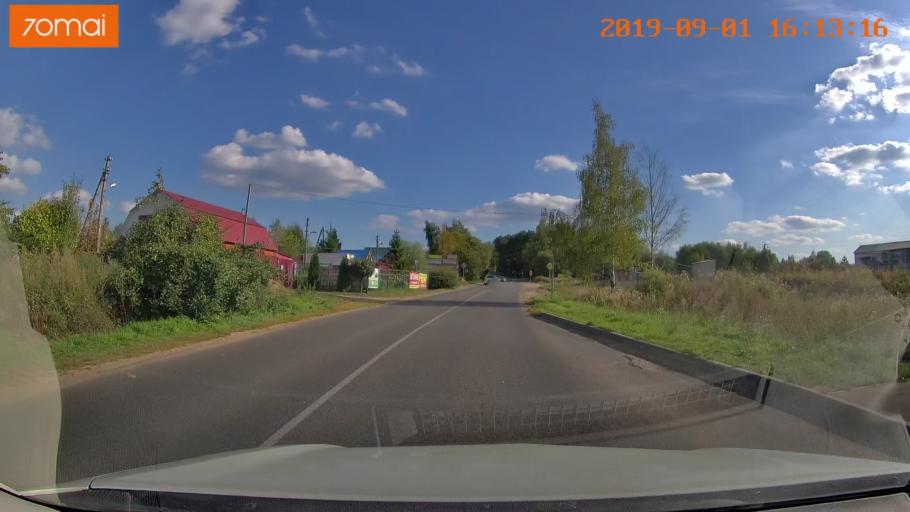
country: RU
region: Kaluga
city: Maloyaroslavets
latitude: 54.9423
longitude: 36.4591
